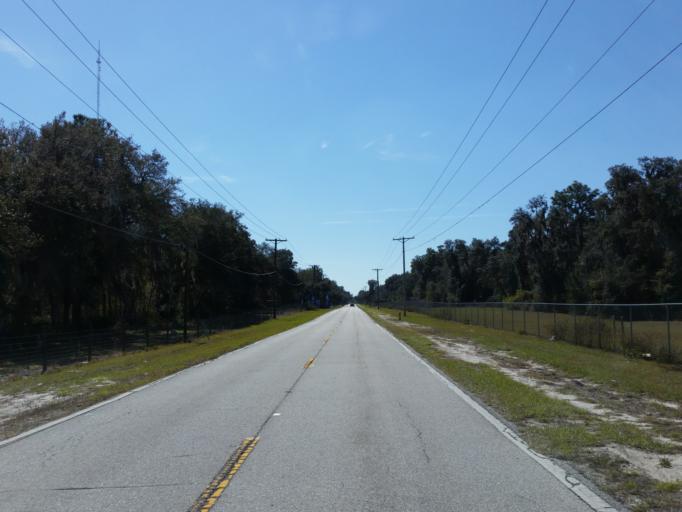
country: US
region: Florida
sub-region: Hillsborough County
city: Boyette
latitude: 27.8301
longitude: -82.2445
